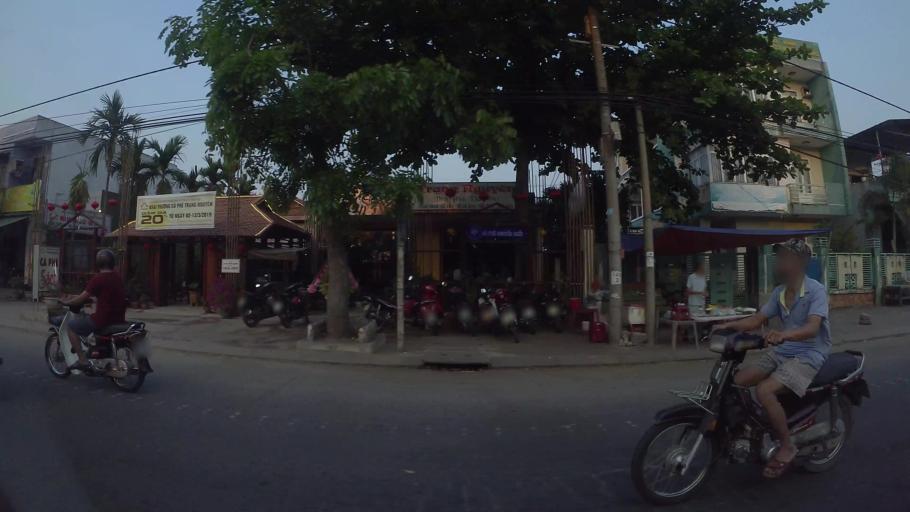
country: VN
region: Da Nang
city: Cam Le
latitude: 15.9563
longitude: 108.2161
